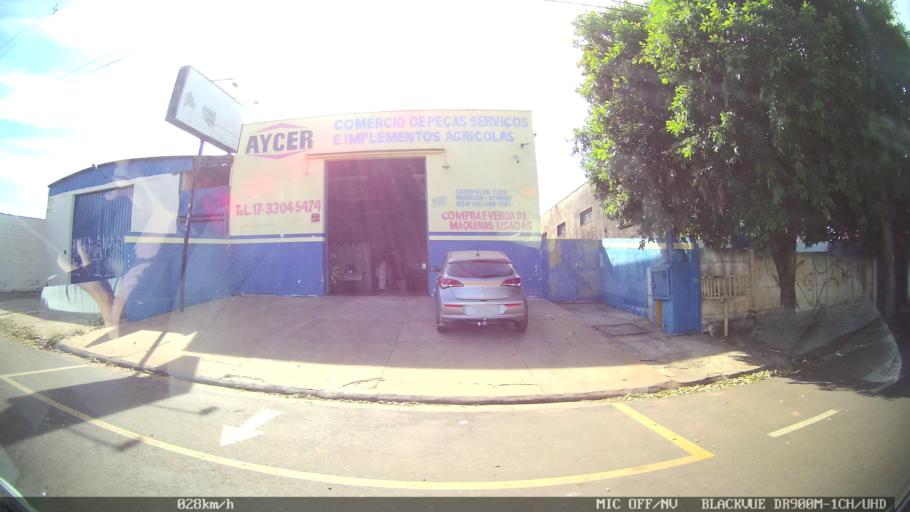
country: BR
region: Sao Paulo
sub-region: Sao Jose Do Rio Preto
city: Sao Jose do Rio Preto
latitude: -20.8502
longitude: -49.3828
